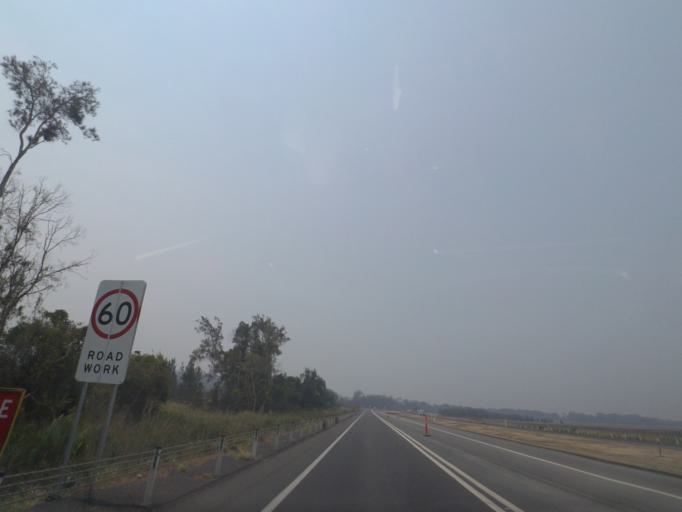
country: AU
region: New South Wales
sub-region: Ballina
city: Ballina
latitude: -28.8729
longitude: 153.4900
